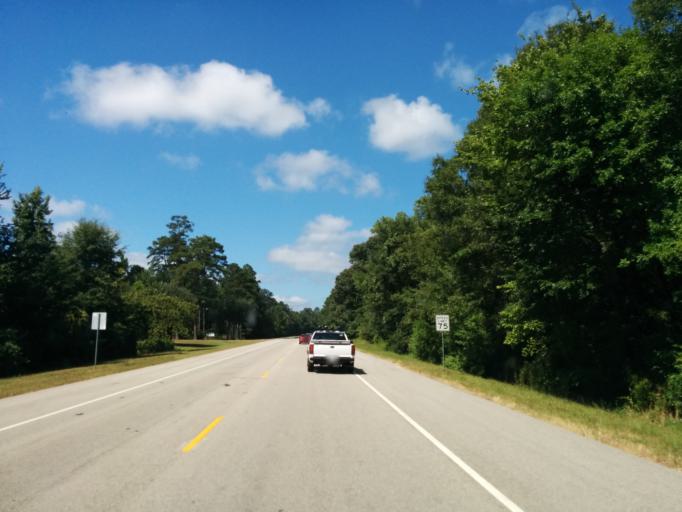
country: US
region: Texas
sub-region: Angelina County
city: Hudson
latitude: 31.3897
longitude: -94.9763
